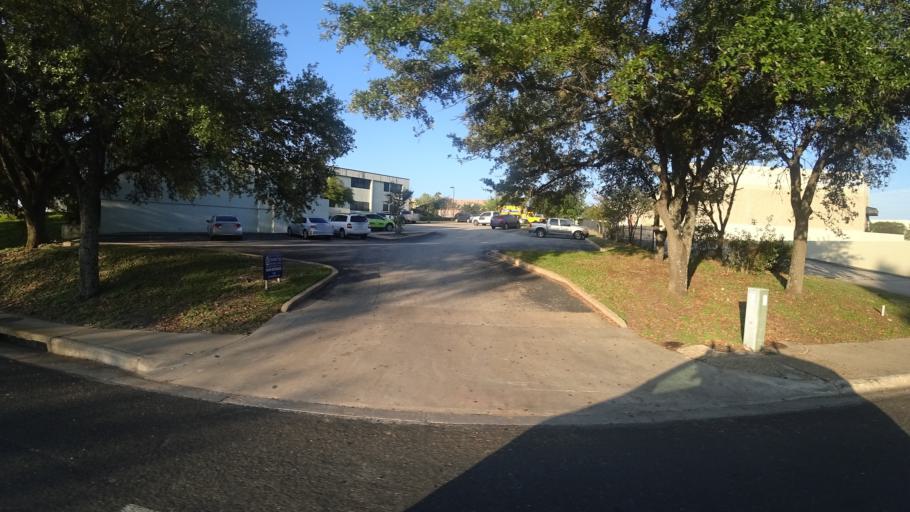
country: US
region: Texas
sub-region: Travis County
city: Austin
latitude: 30.3352
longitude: -97.6806
